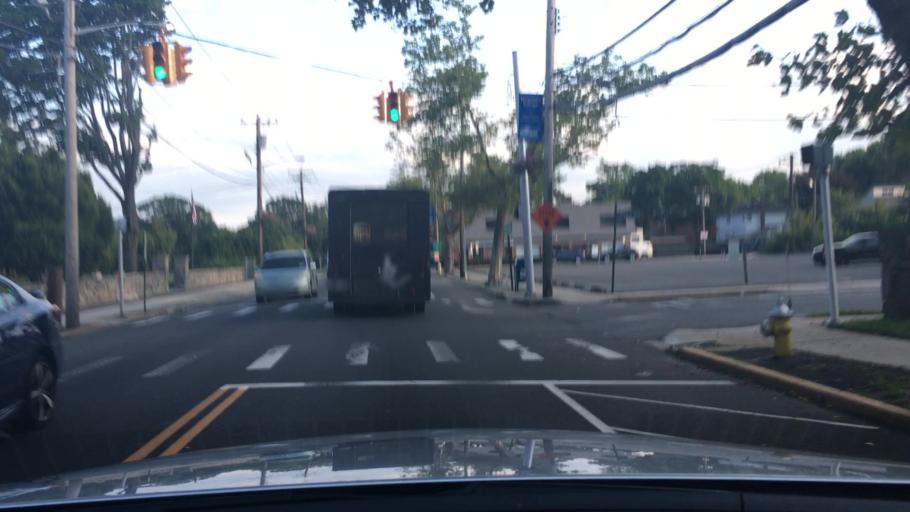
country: US
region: New York
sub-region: Nassau County
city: Westbury
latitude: 40.7508
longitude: -73.5878
